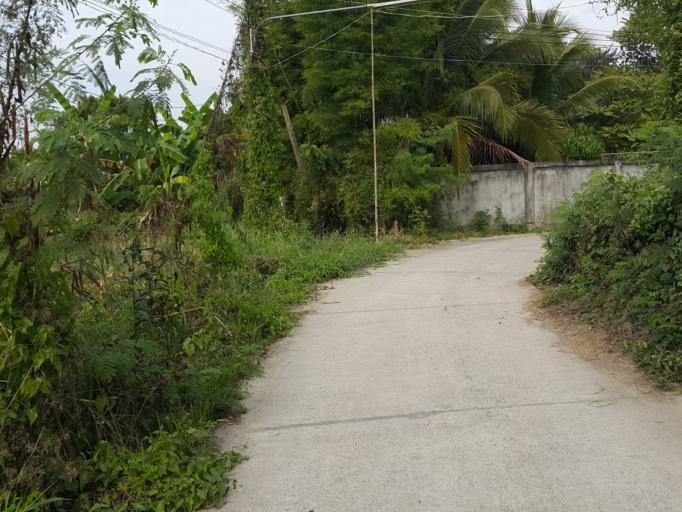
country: TH
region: Chiang Mai
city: San Kamphaeng
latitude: 18.8259
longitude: 99.1402
